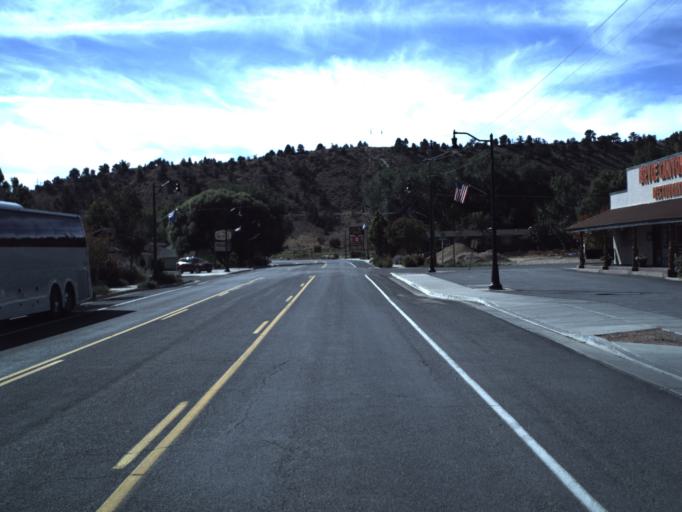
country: US
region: Utah
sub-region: Garfield County
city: Panguitch
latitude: 37.6245
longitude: -112.0818
